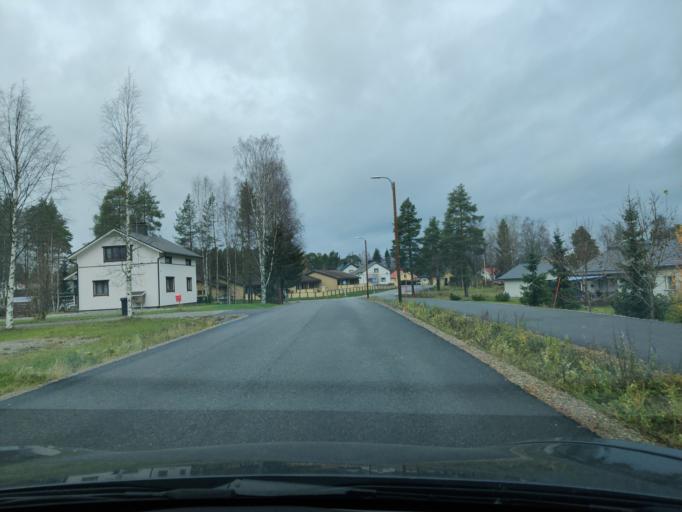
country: FI
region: Northern Savo
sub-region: Ylae-Savo
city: Kiuruvesi
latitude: 63.6481
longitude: 26.6370
